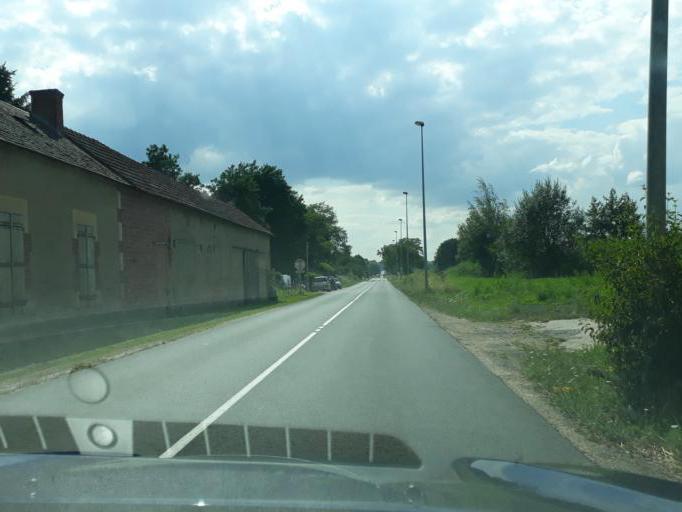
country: FR
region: Bourgogne
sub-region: Departement de la Nievre
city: Fourchambault
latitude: 47.0130
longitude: 3.0623
